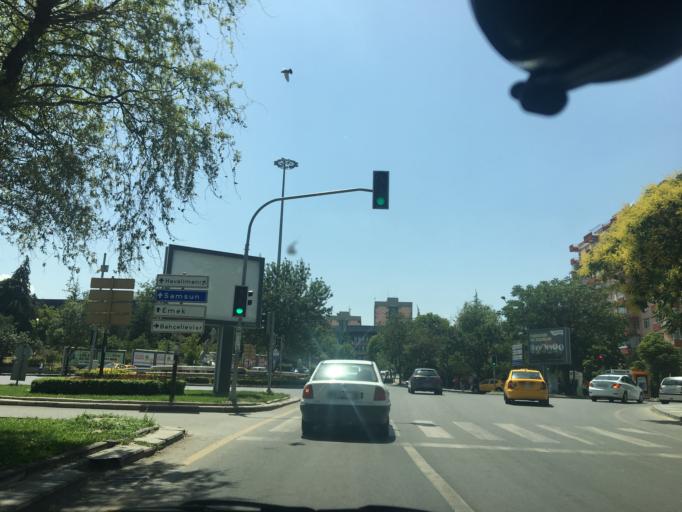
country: TR
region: Ankara
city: Ankara
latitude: 39.9174
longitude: 32.8288
